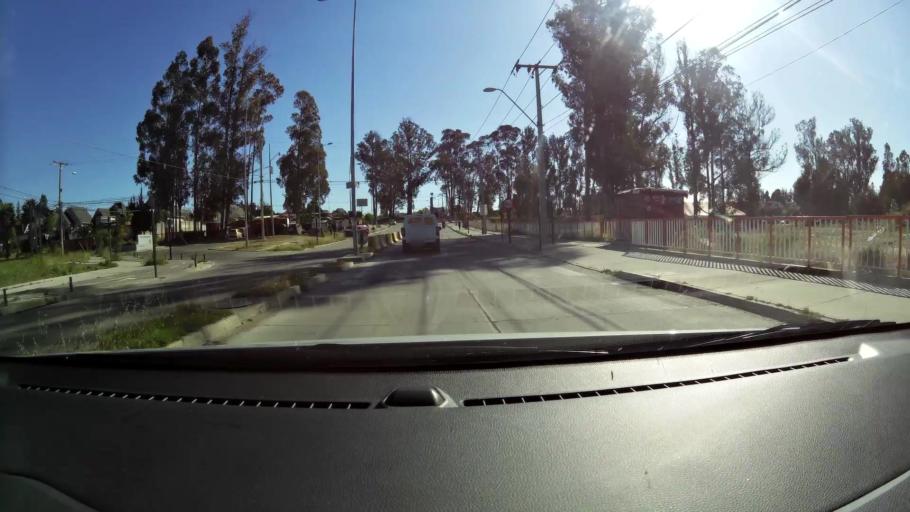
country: CL
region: Valparaiso
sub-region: Provincia de Valparaiso
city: Vina del Mar
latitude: -33.1187
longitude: -71.5719
